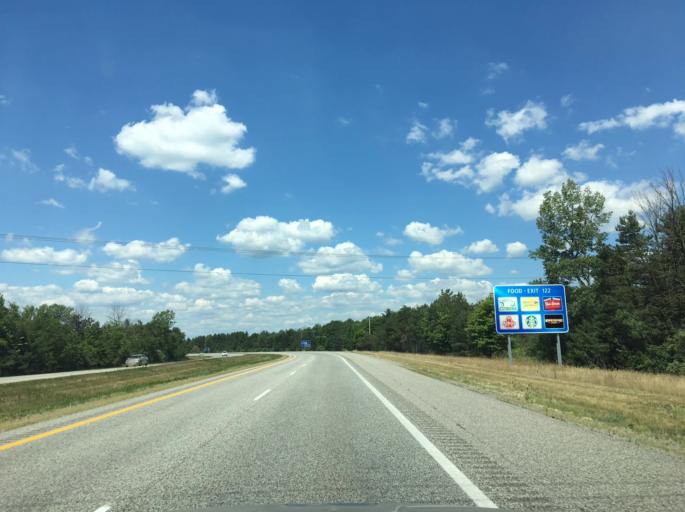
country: US
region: Michigan
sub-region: Midland County
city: Midland
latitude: 43.6540
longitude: -84.2063
